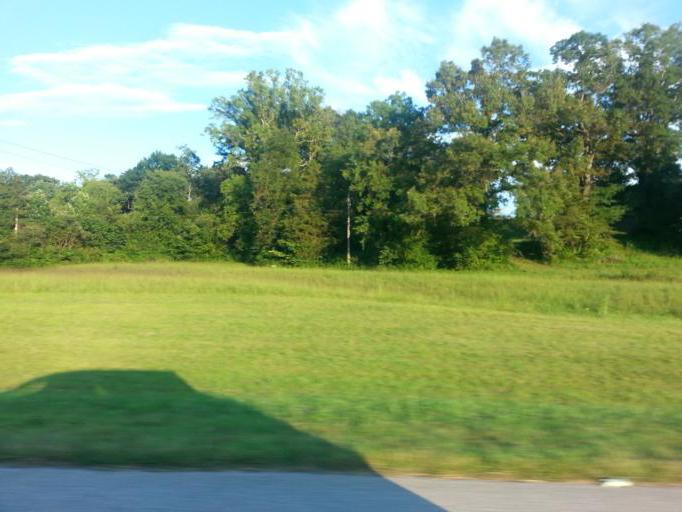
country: US
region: Tennessee
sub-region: Knox County
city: Mascot
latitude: 36.0801
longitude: -83.7663
